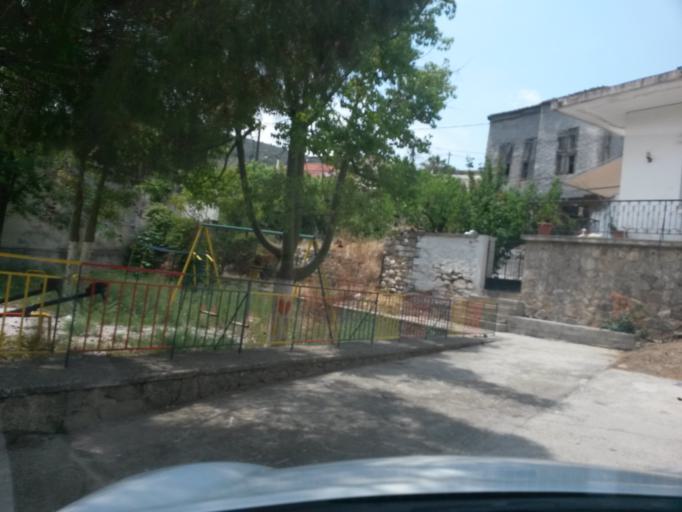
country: GR
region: North Aegean
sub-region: Nomos Lesvou
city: Agiasos
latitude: 39.1839
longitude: 26.4072
